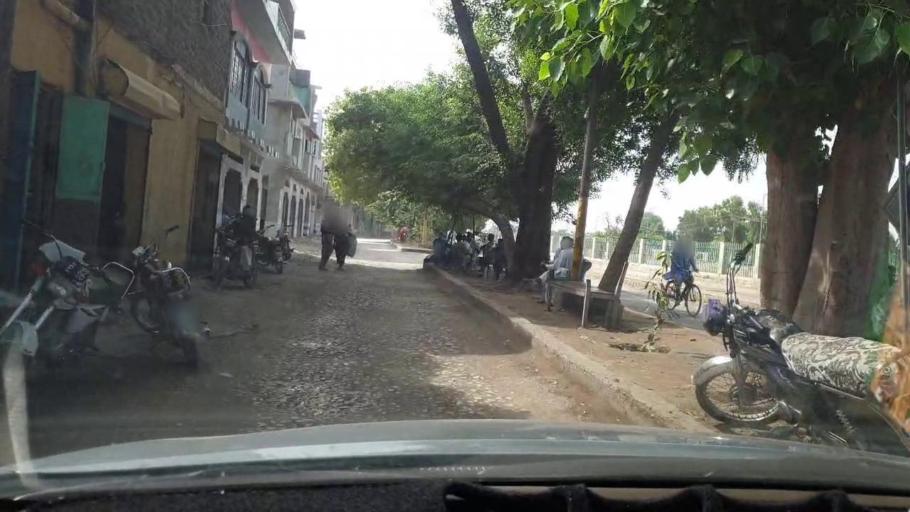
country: PK
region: Sindh
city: Khairpur
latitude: 27.5248
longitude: 68.7556
